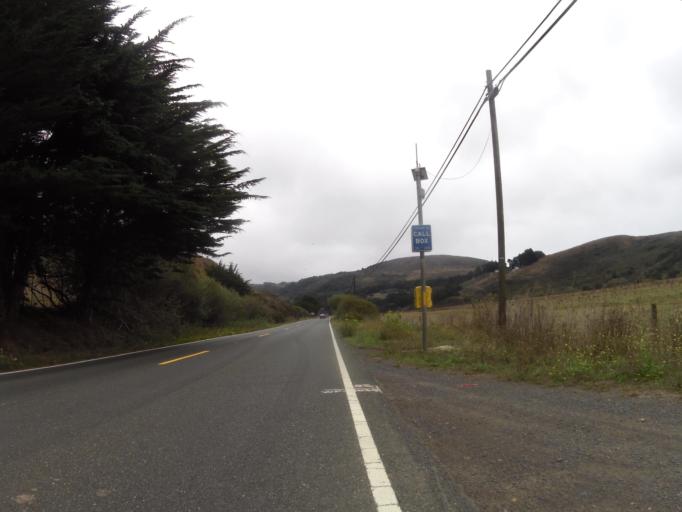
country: US
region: California
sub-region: Sonoma County
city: Monte Rio
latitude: 38.4410
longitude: -123.1087
